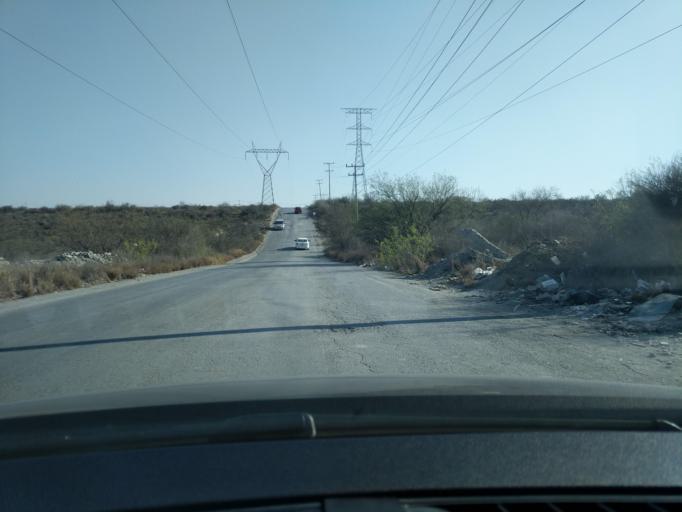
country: MX
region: Coahuila
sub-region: Ramos Arizpe
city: Ramos Arizpe
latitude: 25.5375
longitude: -100.9781
